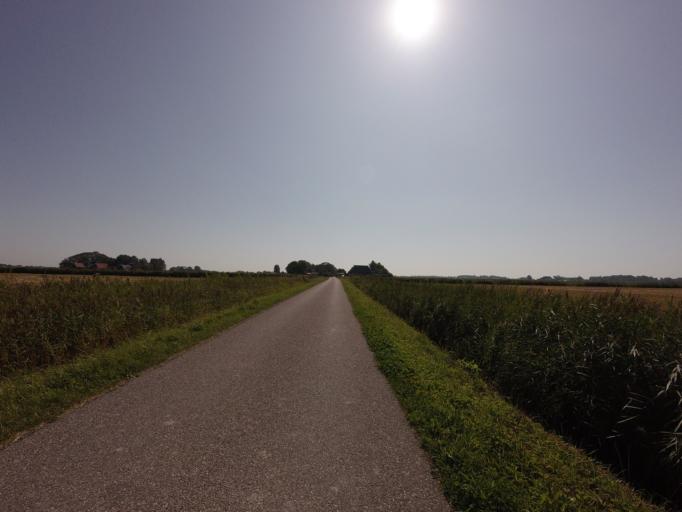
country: NL
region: Friesland
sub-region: Gemeente Dongeradeel
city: Holwerd
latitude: 53.3688
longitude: 5.9206
